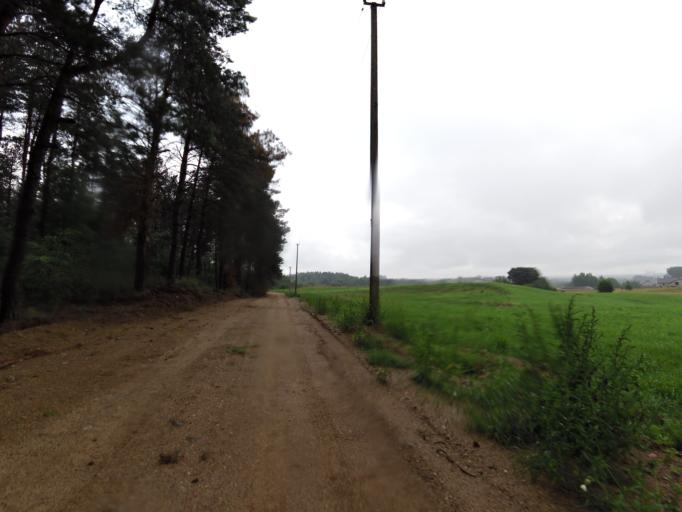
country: LT
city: Grigiskes
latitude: 54.7120
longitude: 25.1107
